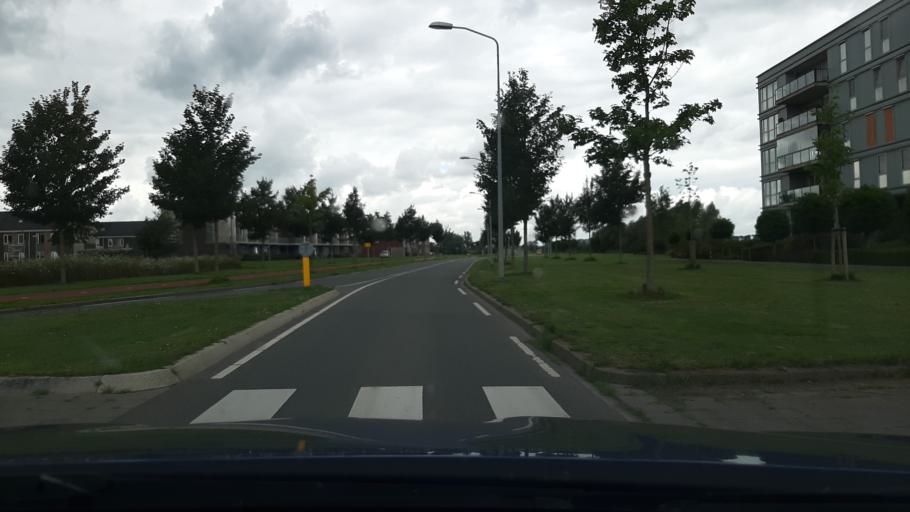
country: NL
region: Flevoland
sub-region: Gemeente Zeewolde
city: Zeewolde
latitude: 52.3458
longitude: 5.5251
